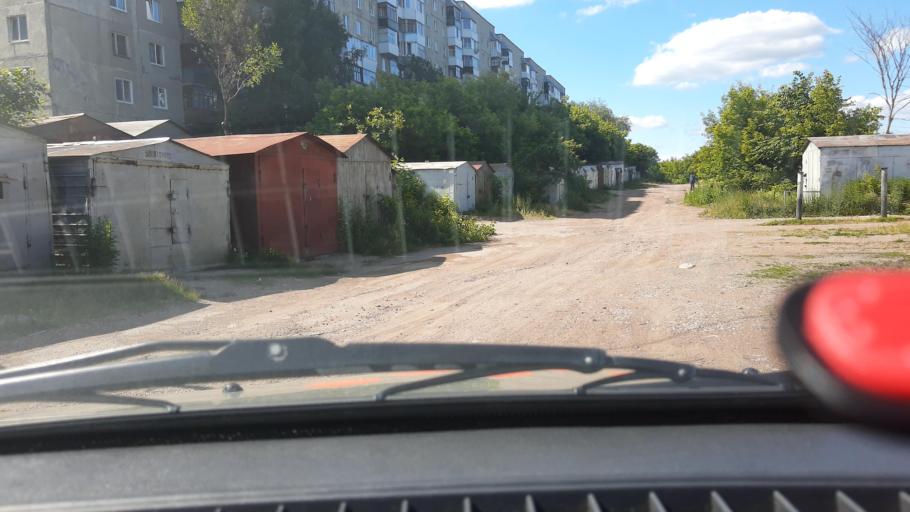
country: RU
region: Bashkortostan
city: Ufa
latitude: 54.8181
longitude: 56.1319
